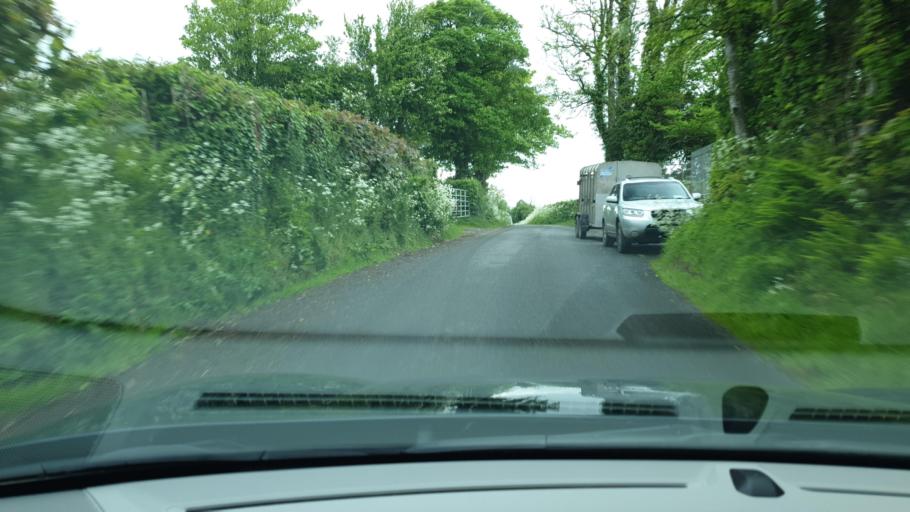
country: IE
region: Leinster
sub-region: Laois
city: Portlaoise
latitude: 53.0370
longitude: -7.3385
